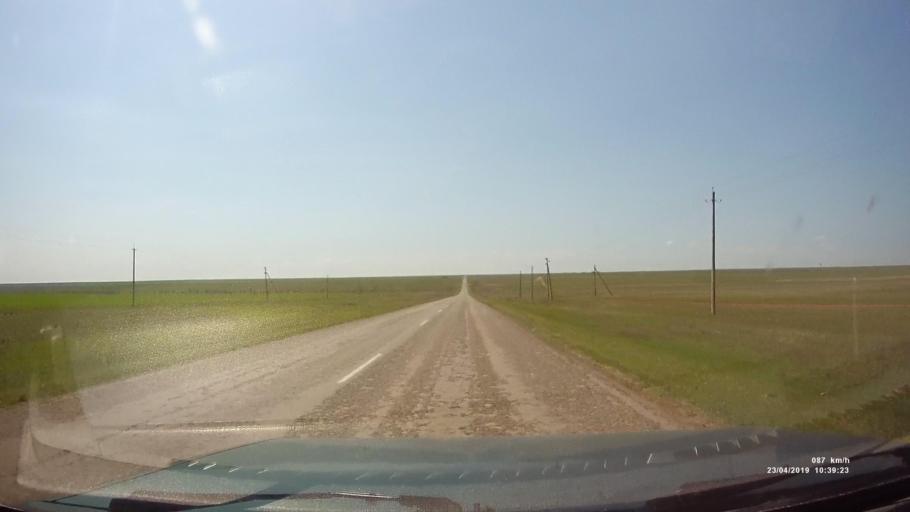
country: RU
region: Kalmykiya
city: Yashalta
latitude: 46.5200
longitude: 42.6387
